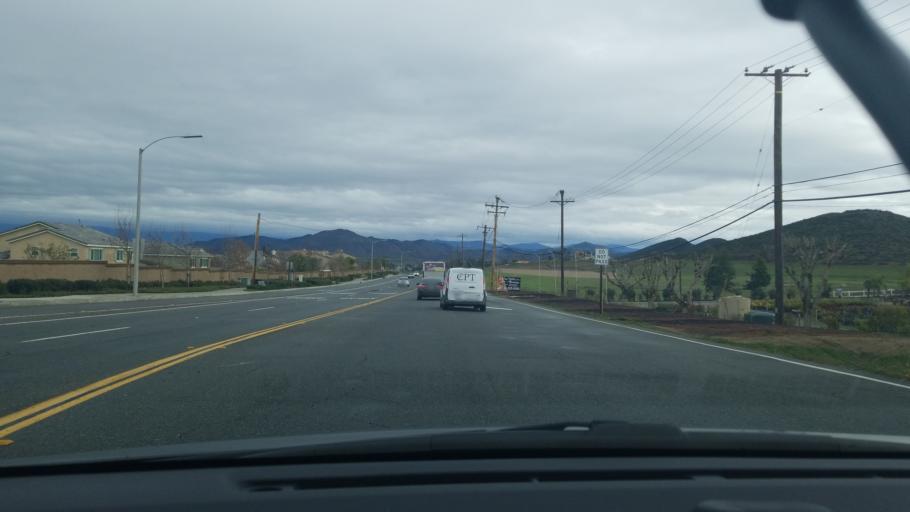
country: US
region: California
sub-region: Riverside County
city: Winchester
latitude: 33.6415
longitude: -117.1358
